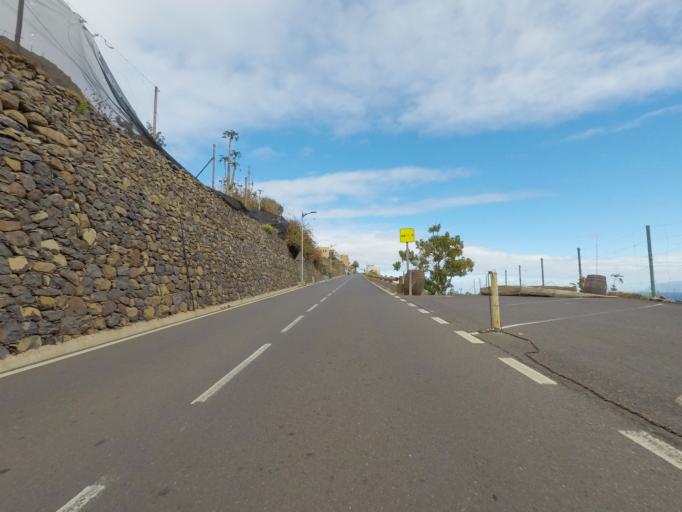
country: ES
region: Canary Islands
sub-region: Provincia de Santa Cruz de Tenerife
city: Hermigua
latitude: 28.1766
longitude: -17.1861
